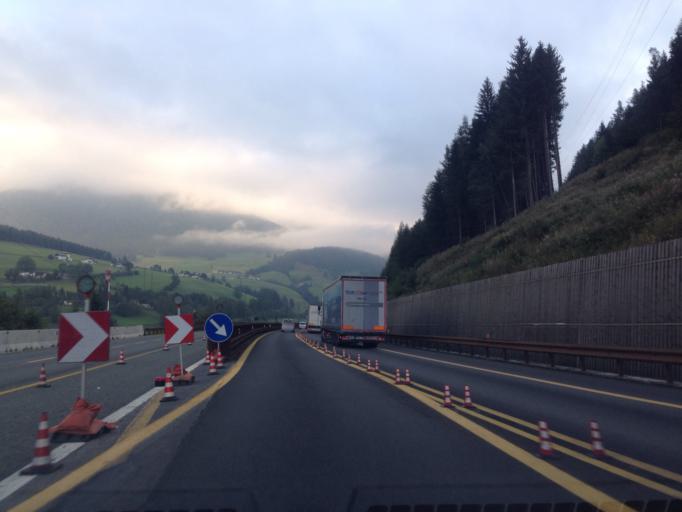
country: IT
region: Trentino-Alto Adige
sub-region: Bolzano
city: Colle Isarco
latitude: 46.9391
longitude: 11.4492
